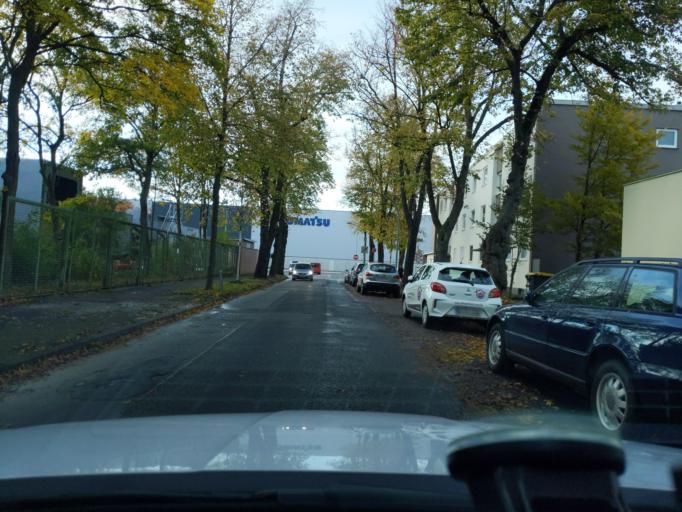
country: DE
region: North Rhine-Westphalia
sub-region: Regierungsbezirk Dusseldorf
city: Hilden
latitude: 51.1698
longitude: 6.8795
